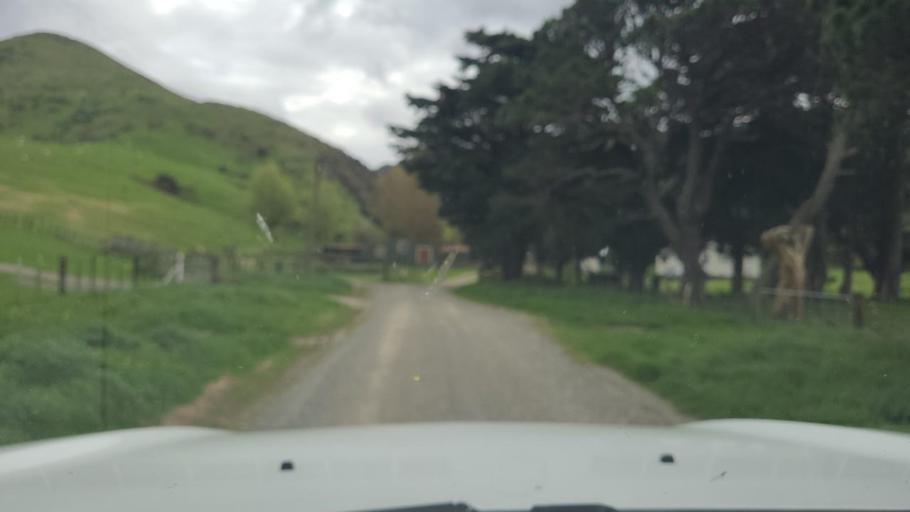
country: NZ
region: Wellington
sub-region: Masterton District
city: Masterton
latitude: -40.9668
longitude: 175.4897
